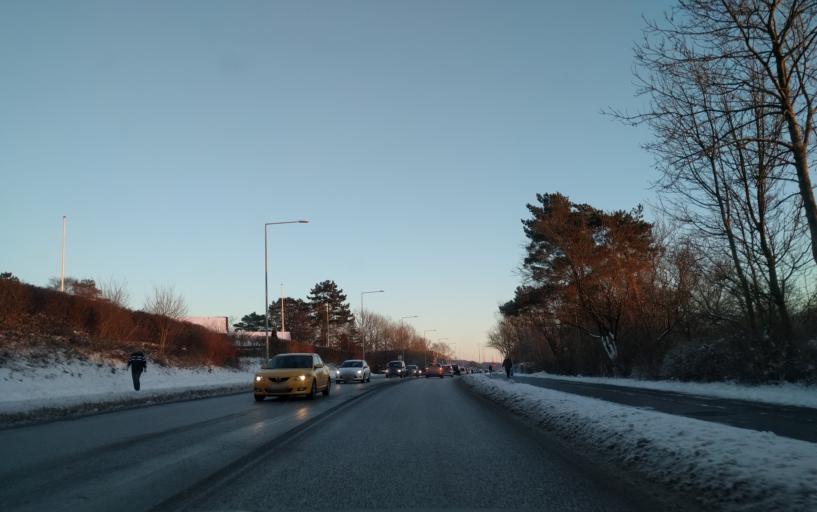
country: DK
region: North Denmark
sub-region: Alborg Kommune
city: Aalborg
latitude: 57.0259
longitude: 9.9371
